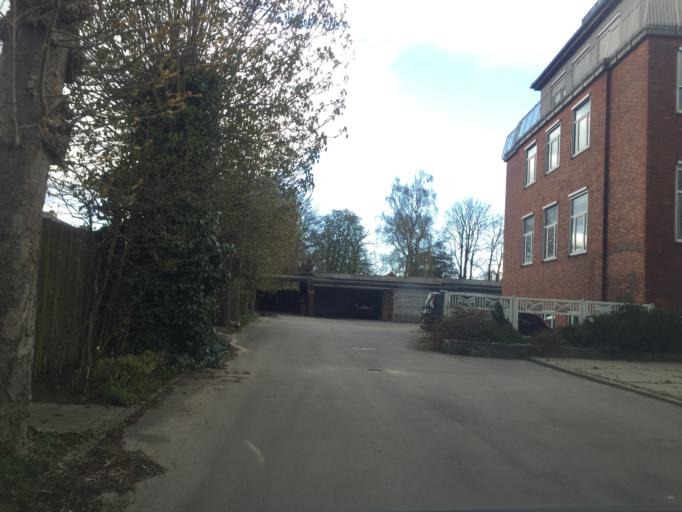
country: DK
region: Capital Region
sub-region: Gentofte Kommune
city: Charlottenlund
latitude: 55.7620
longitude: 12.5669
